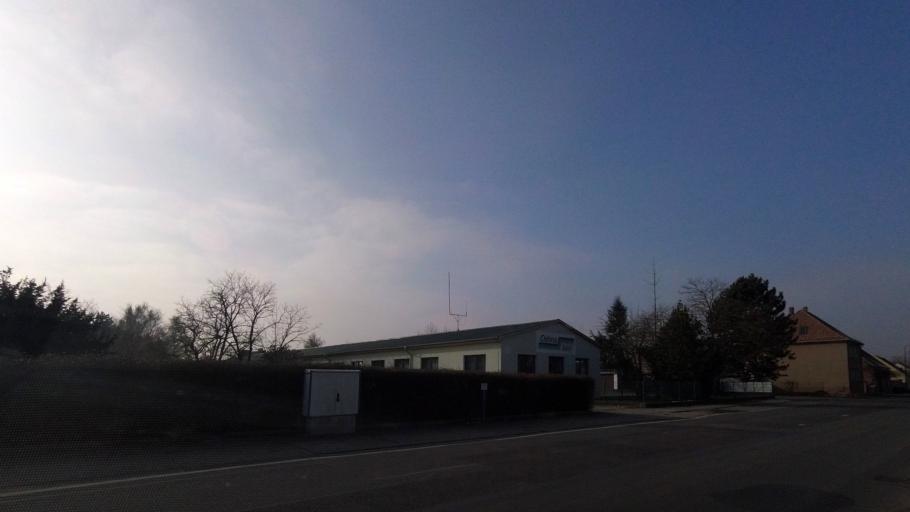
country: DE
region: Brandenburg
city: Juterbog
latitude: 51.9288
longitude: 13.0447
